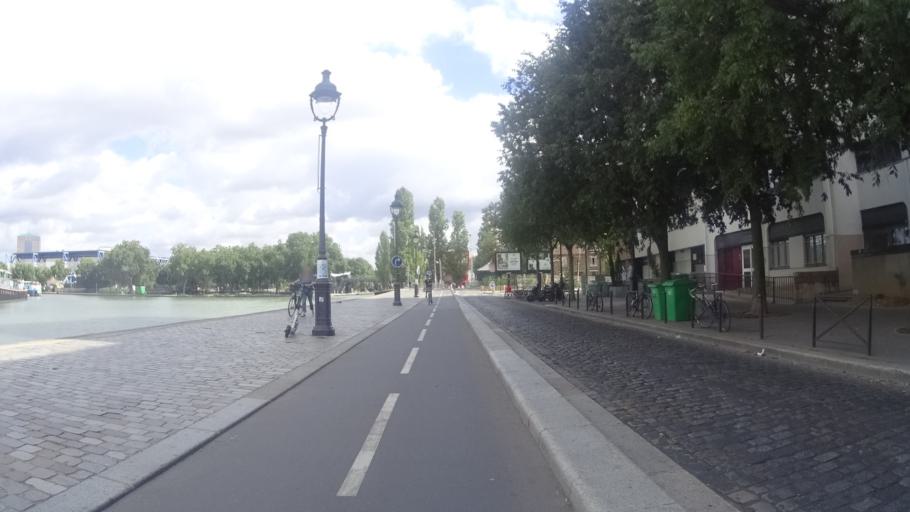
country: FR
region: Ile-de-France
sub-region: Departement de Seine-Saint-Denis
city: Le Pre-Saint-Gervais
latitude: 48.8911
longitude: 2.3854
